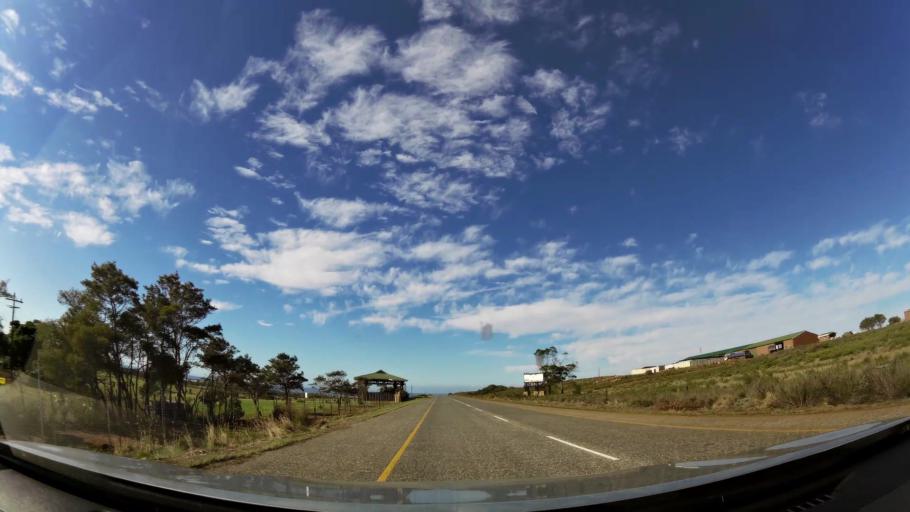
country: ZA
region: Eastern Cape
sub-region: Cacadu District Municipality
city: Jeffrey's Bay
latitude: -34.0181
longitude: 24.8896
